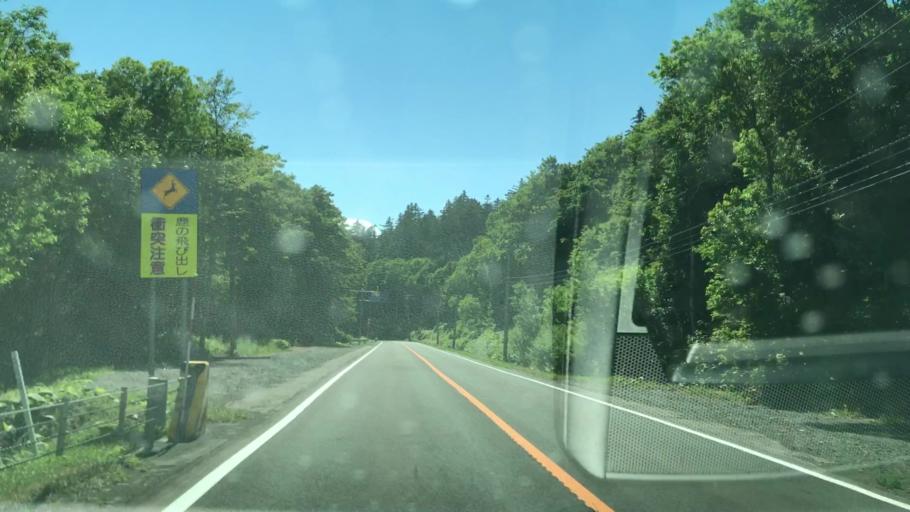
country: JP
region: Hokkaido
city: Shimo-furano
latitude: 42.9722
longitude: 142.6796
